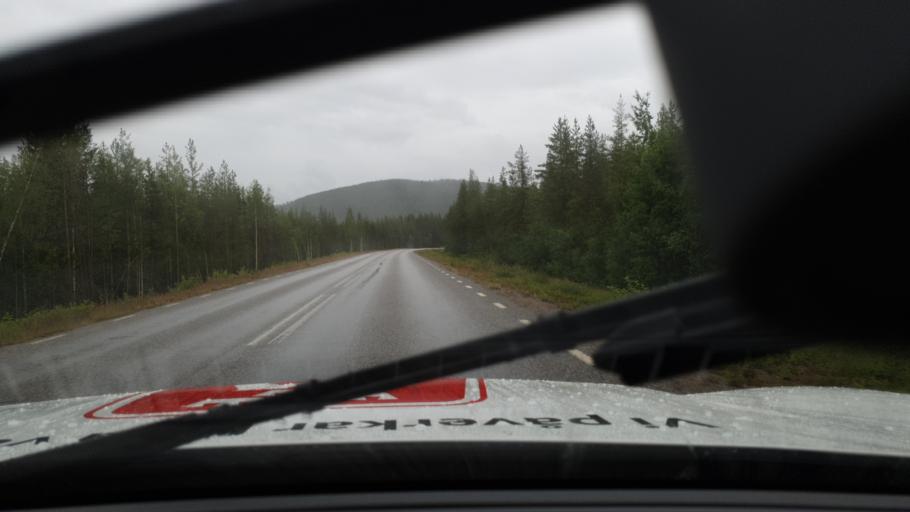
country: SE
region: Norrbotten
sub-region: Jokkmokks Kommun
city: Jokkmokk
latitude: 66.4660
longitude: 20.4495
